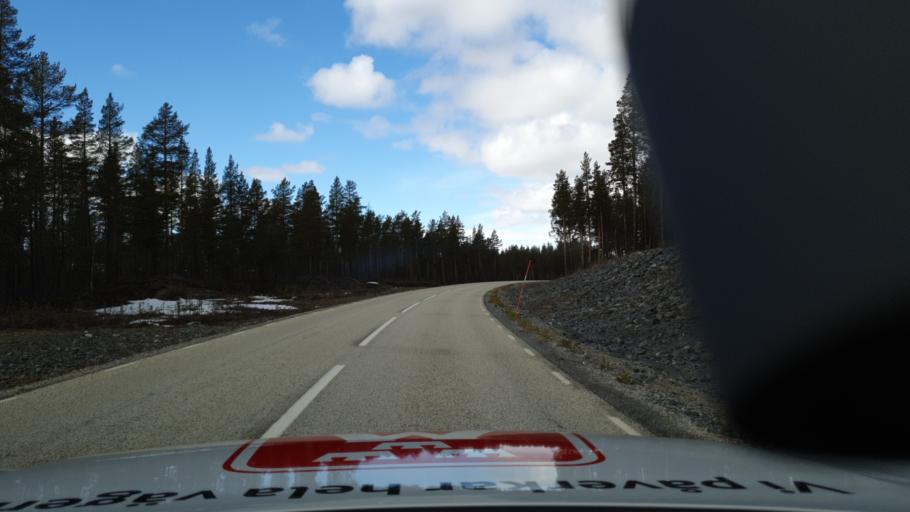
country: SE
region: Jaemtland
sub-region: Are Kommun
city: Jarpen
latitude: 62.8376
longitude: 13.4167
